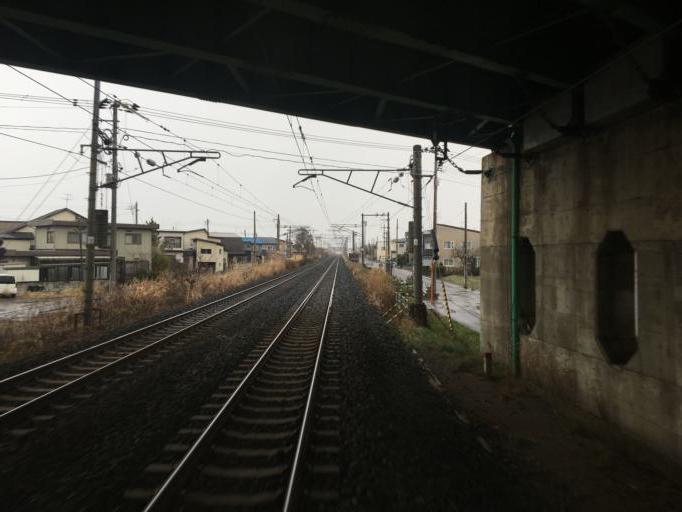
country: JP
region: Aomori
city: Aomori Shi
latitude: 40.8275
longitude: 140.8043
